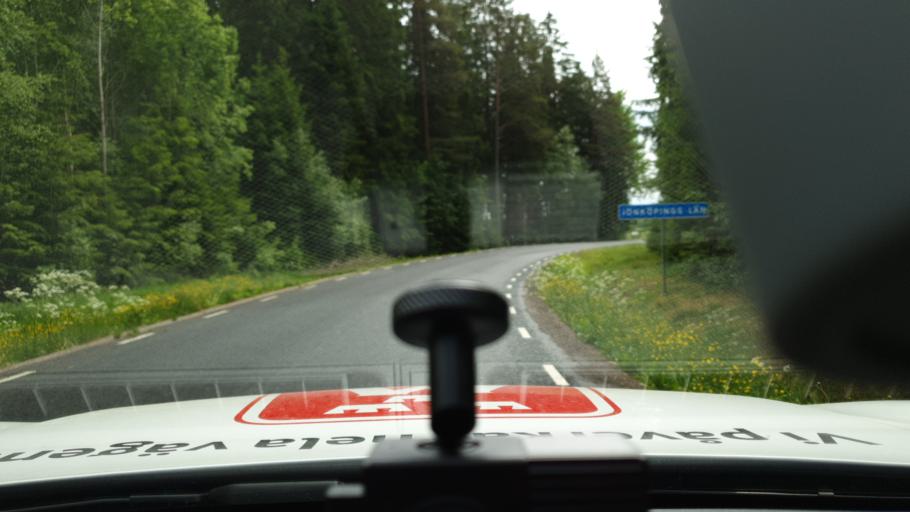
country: SE
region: Joenkoeping
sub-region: Mullsjo Kommun
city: Mullsjoe
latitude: 57.9986
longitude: 13.7320
